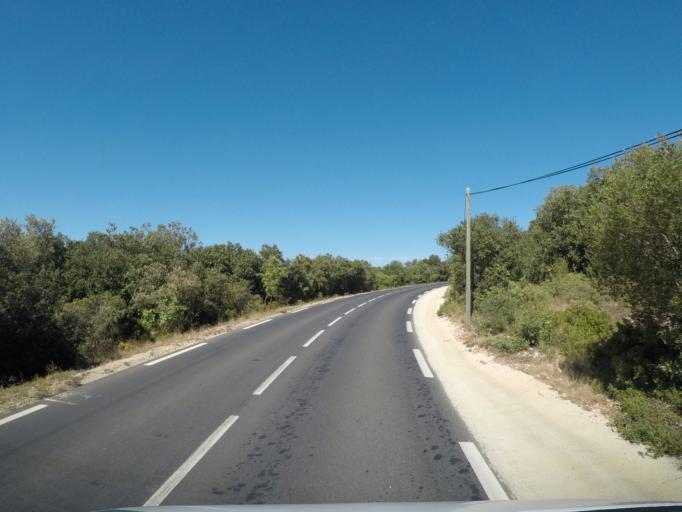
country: FR
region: Languedoc-Roussillon
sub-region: Departement de l'Herault
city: Aniane
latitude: 43.7153
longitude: 3.6228
